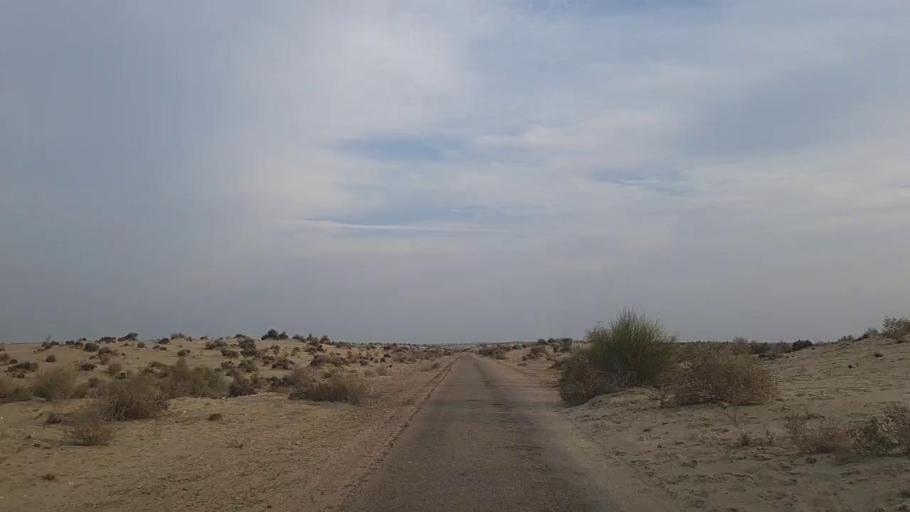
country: PK
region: Sindh
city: Daur
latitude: 26.5083
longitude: 68.5112
